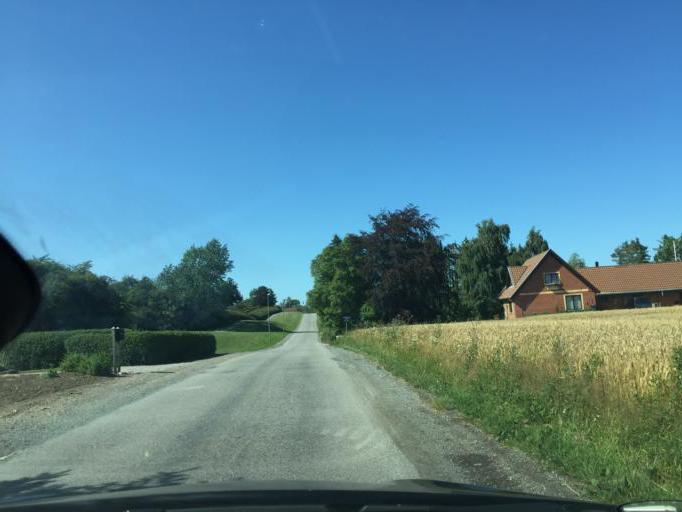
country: DK
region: South Denmark
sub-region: Nordfyns Kommune
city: Sonderso
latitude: 55.4822
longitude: 10.2649
